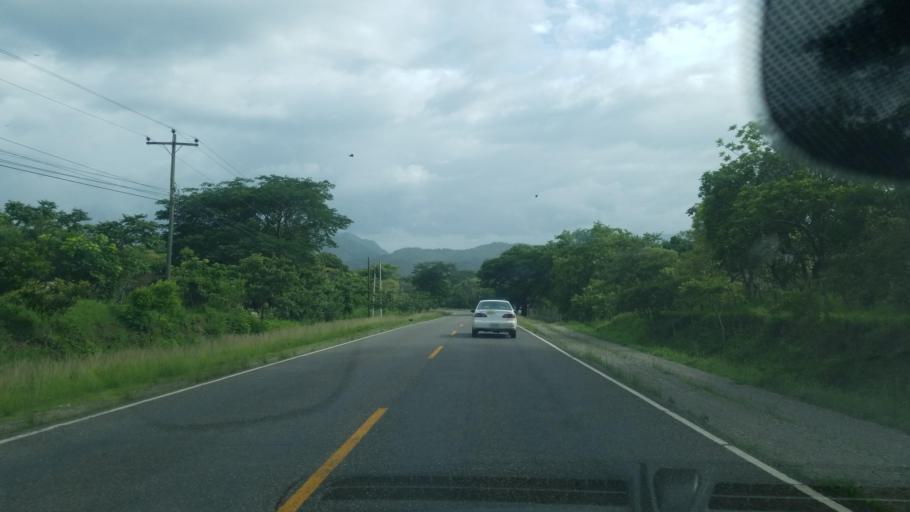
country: HN
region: Ocotepeque
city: Antigua Ocotepeque
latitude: 14.3884
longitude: -89.2055
